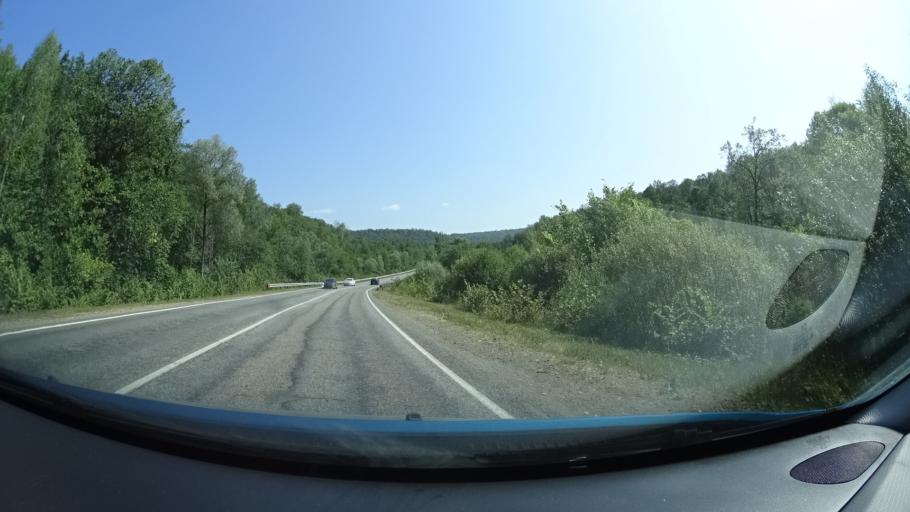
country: RU
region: Bashkortostan
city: Inzer
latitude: 54.3373
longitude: 57.1073
